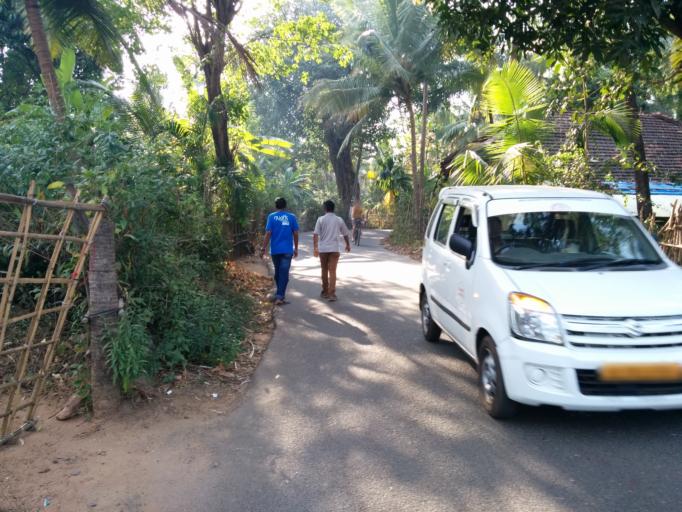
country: IN
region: Goa
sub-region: South Goa
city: Kankon
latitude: 15.0101
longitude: 74.0290
